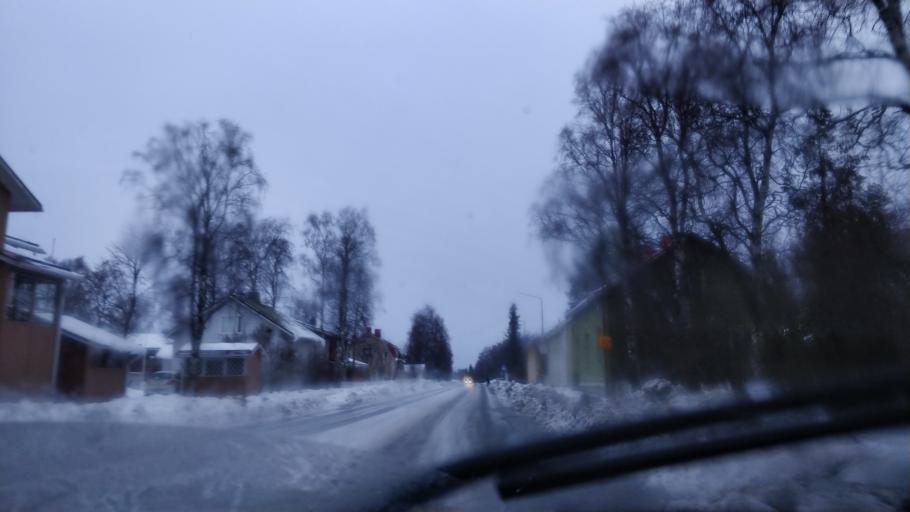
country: FI
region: Lapland
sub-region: Kemi-Tornio
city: Kemi
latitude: 65.7396
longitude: 24.5609
